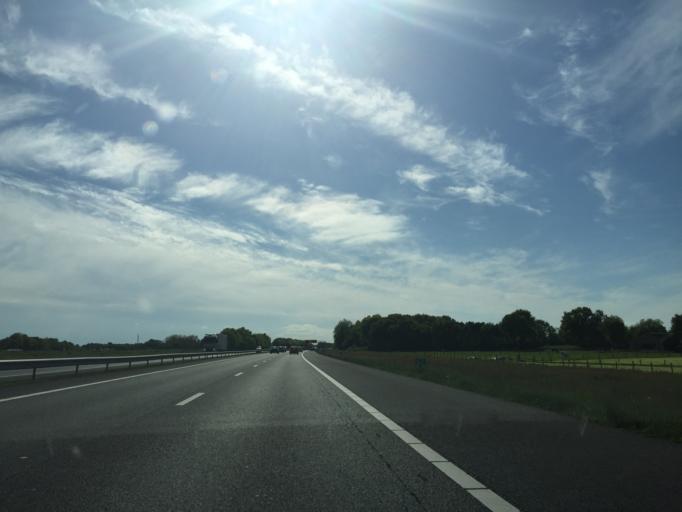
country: NL
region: Gelderland
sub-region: Gemeente Barneveld
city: Voorthuizen
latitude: 52.1721
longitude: 5.6316
